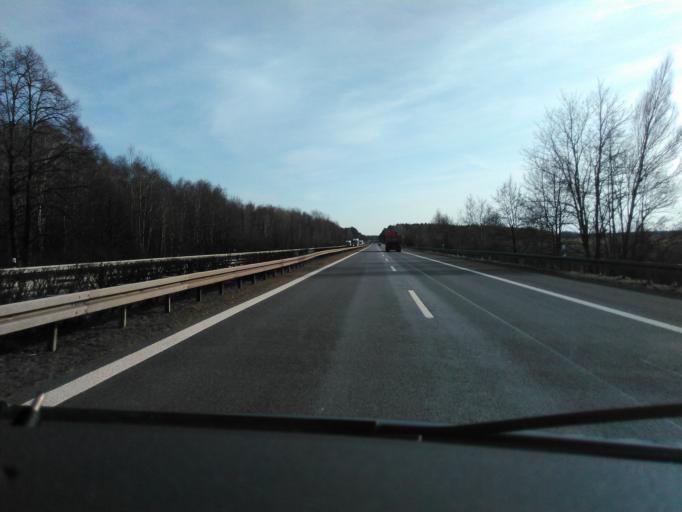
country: DE
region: Brandenburg
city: Bronkow
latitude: 51.6239
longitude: 13.9448
